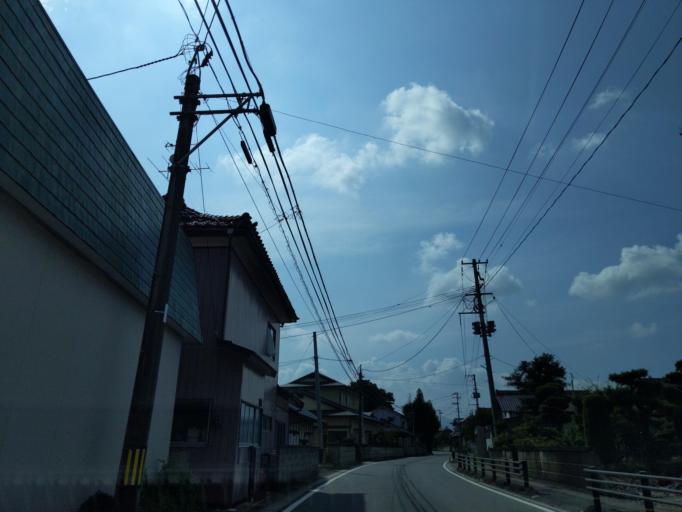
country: JP
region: Fukushima
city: Koriyama
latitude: 37.3622
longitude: 140.3340
